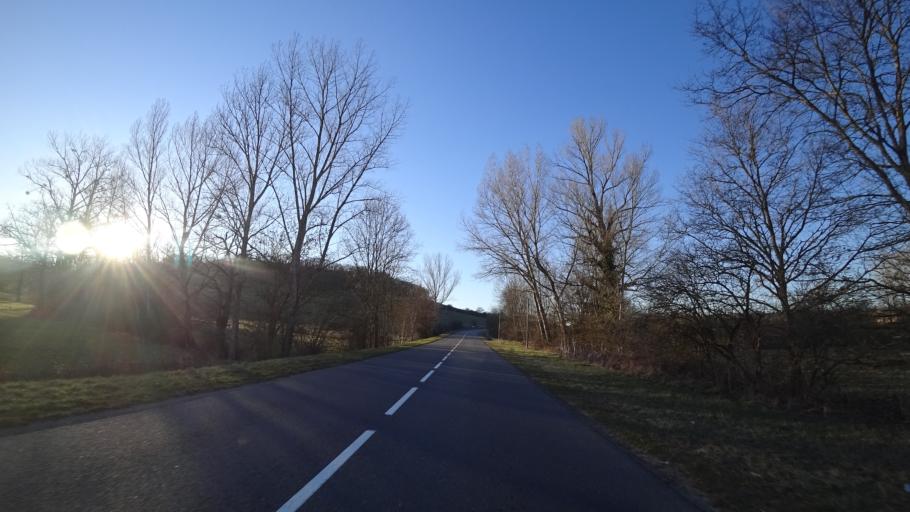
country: FR
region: Midi-Pyrenees
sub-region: Departement de l'Aveyron
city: La Loubiere
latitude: 44.3601
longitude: 2.6490
